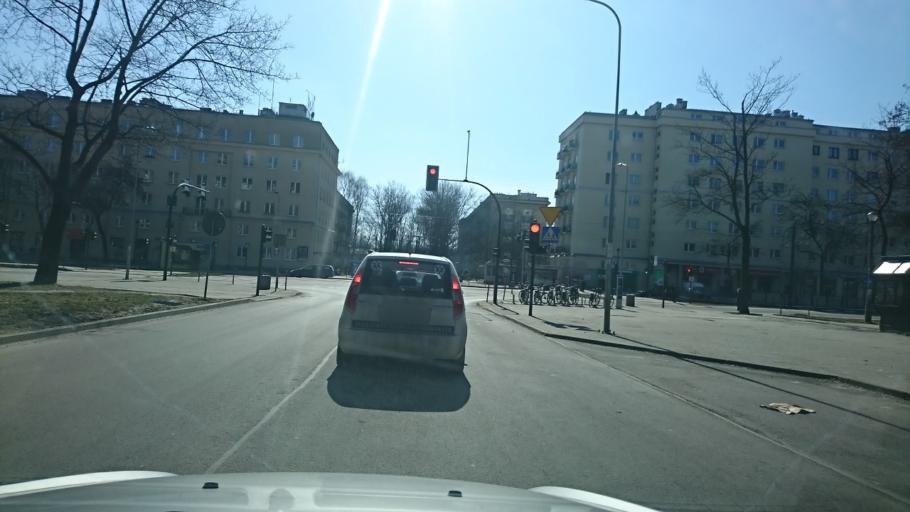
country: PL
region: Lesser Poland Voivodeship
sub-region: Powiat wielicki
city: Kokotow
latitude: 50.0751
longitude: 20.0466
